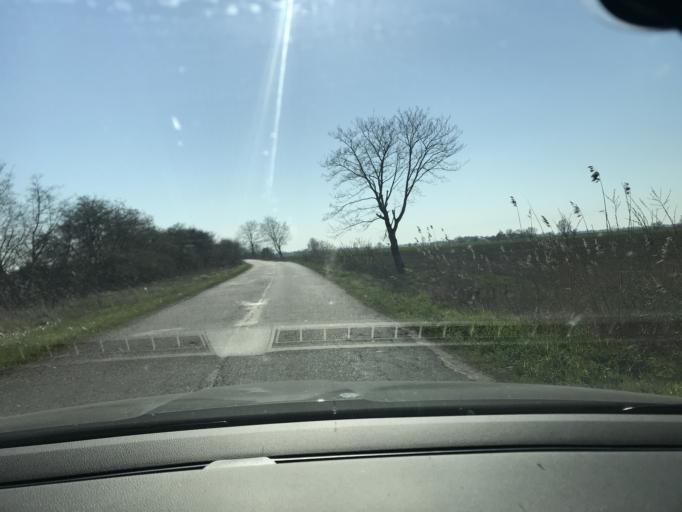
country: PL
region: Pomeranian Voivodeship
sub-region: Powiat nowodworski
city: Sztutowo
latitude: 54.3098
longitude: 19.1564
